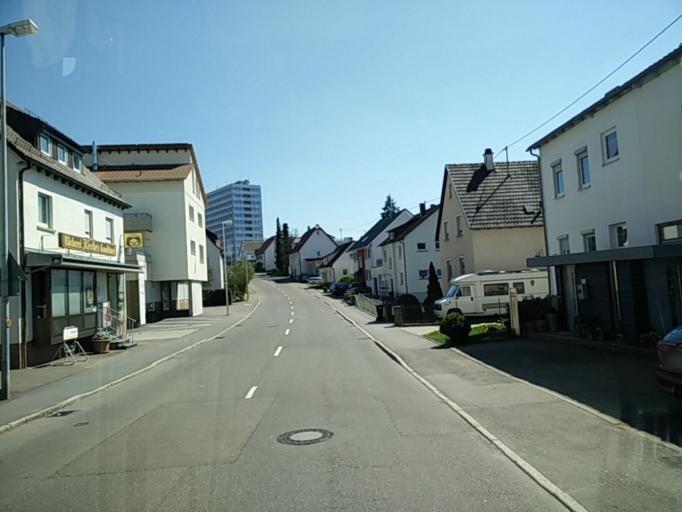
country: DE
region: Baden-Wuerttemberg
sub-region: Tuebingen Region
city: Gomaringen
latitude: 48.4583
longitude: 9.0955
